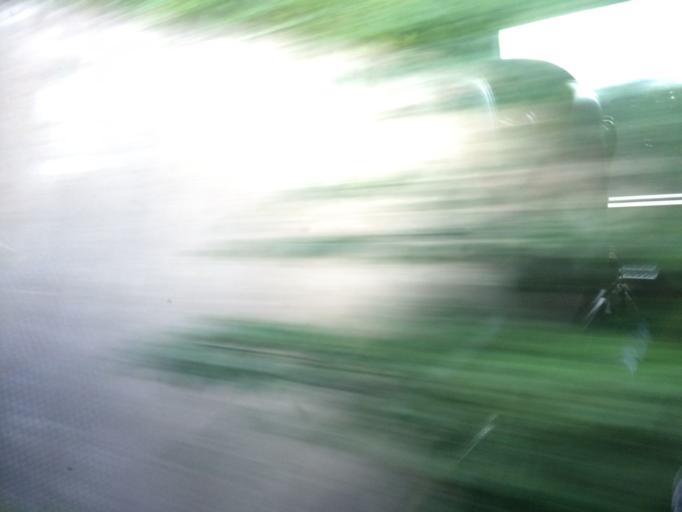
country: GB
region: Scotland
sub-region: Stirling
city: Cowie
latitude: 56.0551
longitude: -3.8469
